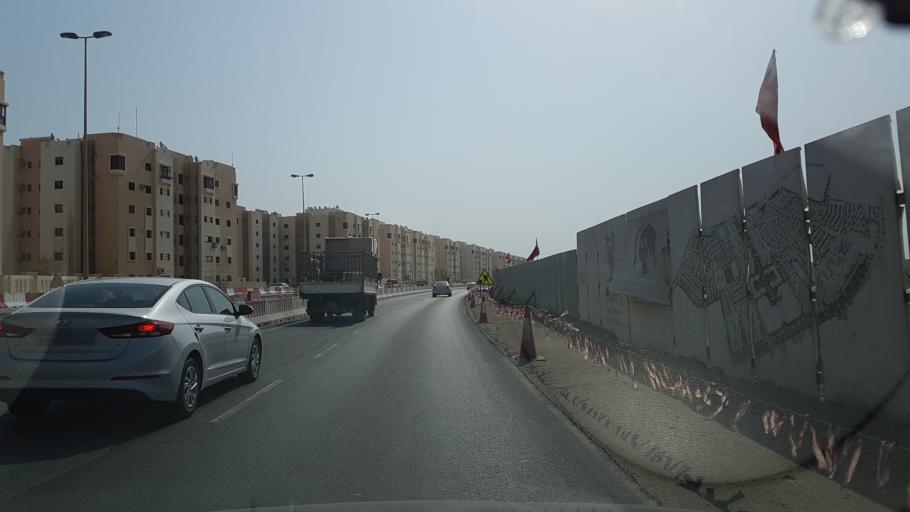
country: BH
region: Northern
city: Madinat `Isa
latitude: 26.1744
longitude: 50.5201
